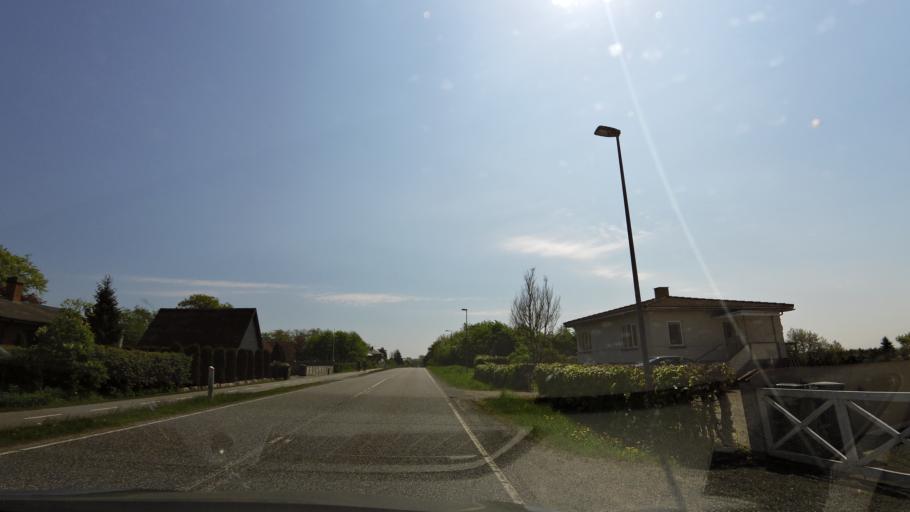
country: DK
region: South Denmark
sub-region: Nyborg Kommune
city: Nyborg
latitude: 55.2423
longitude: 10.7100
